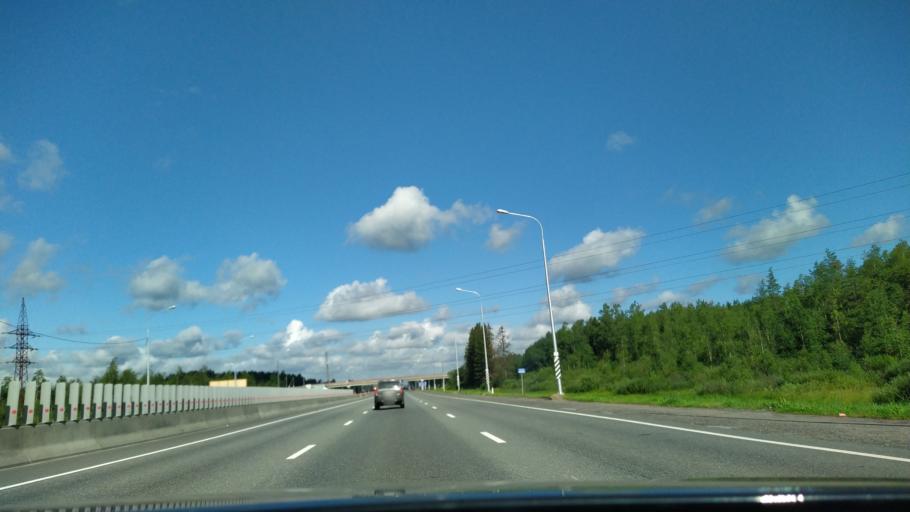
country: RU
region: Leningrad
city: Ul'yanovka
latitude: 59.6031
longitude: 30.7648
